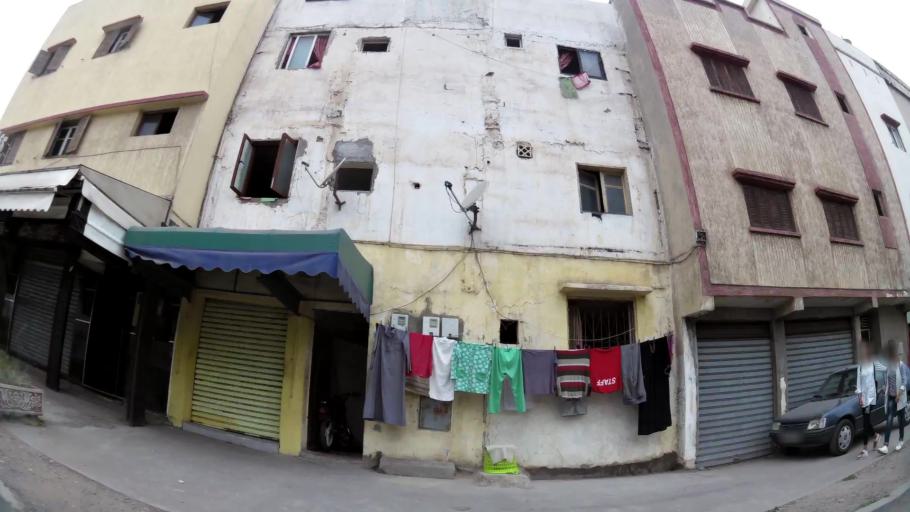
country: MA
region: Rabat-Sale-Zemmour-Zaer
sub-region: Rabat
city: Rabat
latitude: 34.0019
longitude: -6.8672
